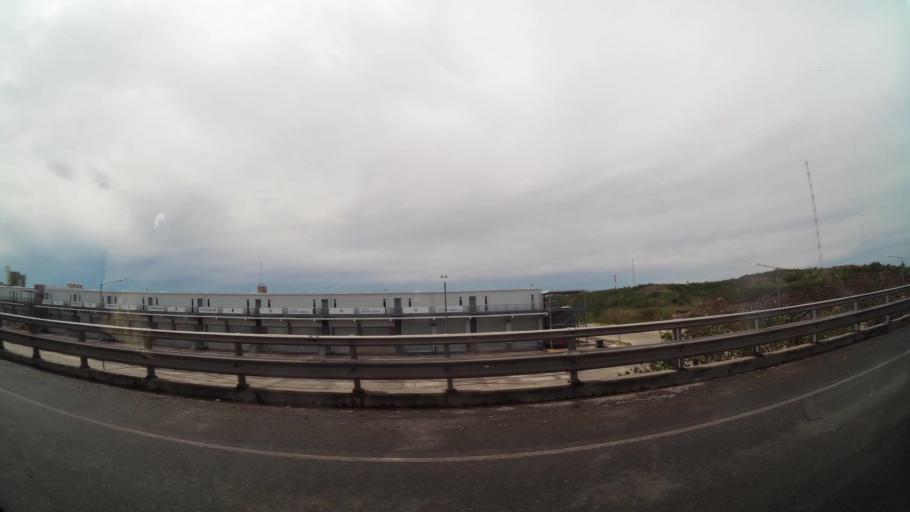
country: AR
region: Buenos Aires F.D.
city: Villa Lugano
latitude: -34.6718
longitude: -58.4394
